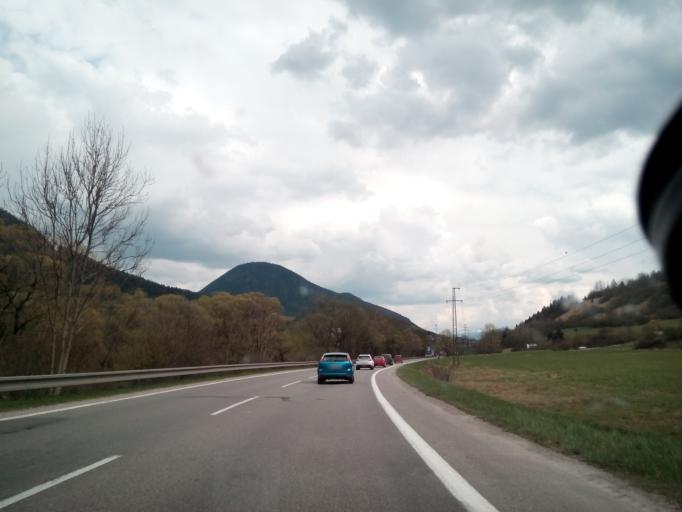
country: SK
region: Zilinsky
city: Ruzomberok
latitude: 49.1101
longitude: 19.2291
